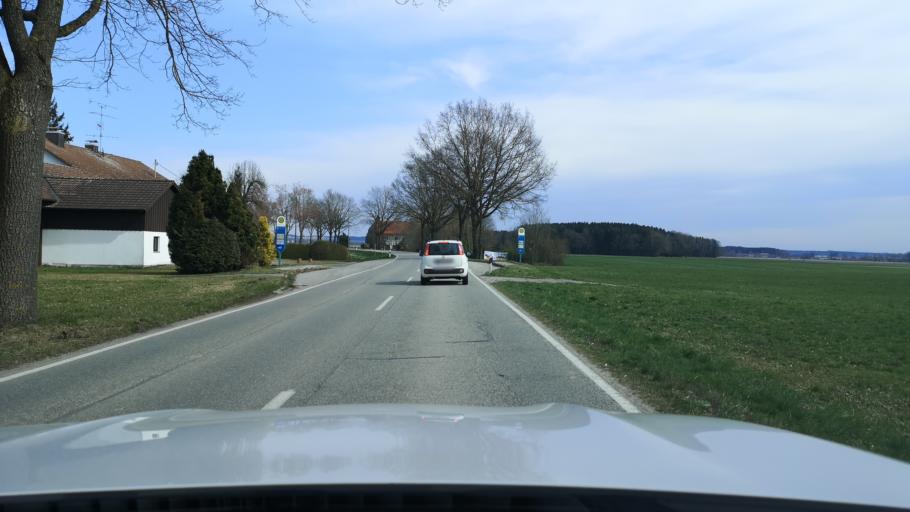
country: DE
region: Bavaria
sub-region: Upper Bavaria
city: Forstinning
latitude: 48.1957
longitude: 11.9094
